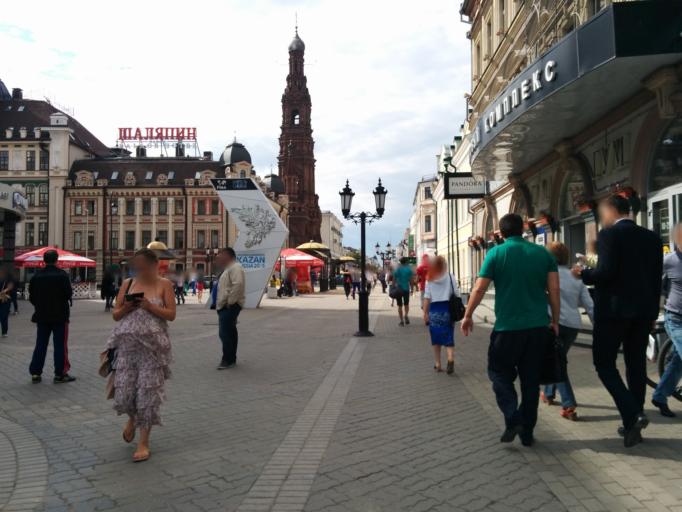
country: RU
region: Tatarstan
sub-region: Gorod Kazan'
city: Kazan
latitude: 55.7876
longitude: 49.1214
